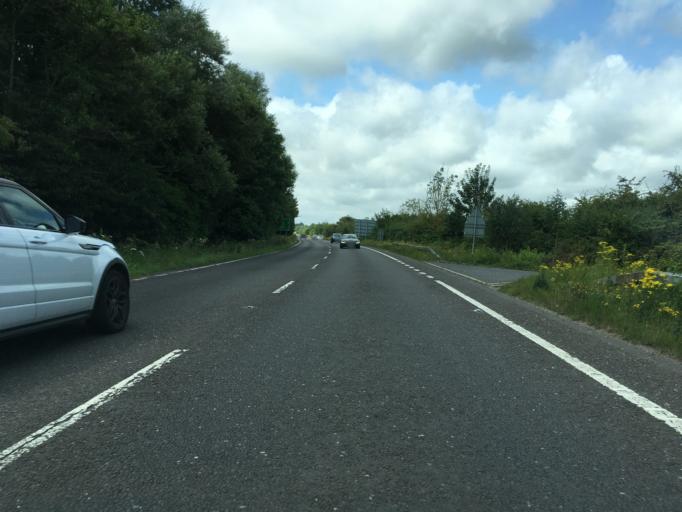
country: GB
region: England
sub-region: East Sussex
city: Pevensey
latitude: 50.8228
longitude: 0.3394
